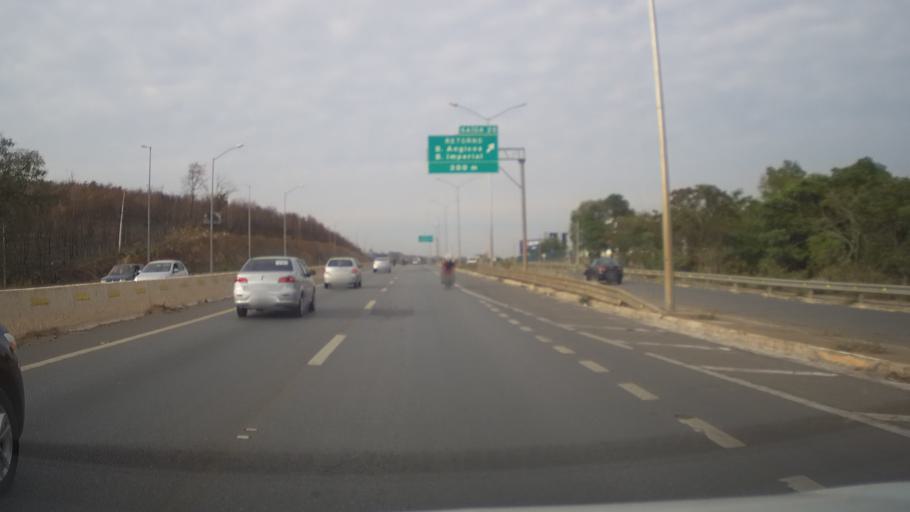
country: BR
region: Minas Gerais
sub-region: Vespasiano
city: Vespasiano
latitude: -19.7141
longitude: -43.9267
